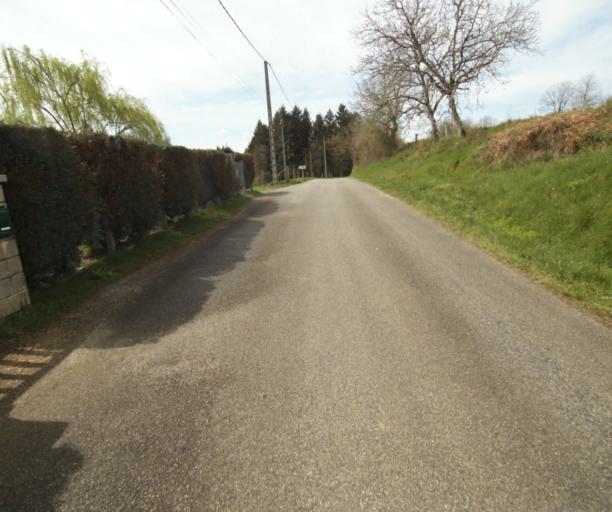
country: FR
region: Limousin
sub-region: Departement de la Correze
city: Laguenne
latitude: 45.2360
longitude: 1.8409
